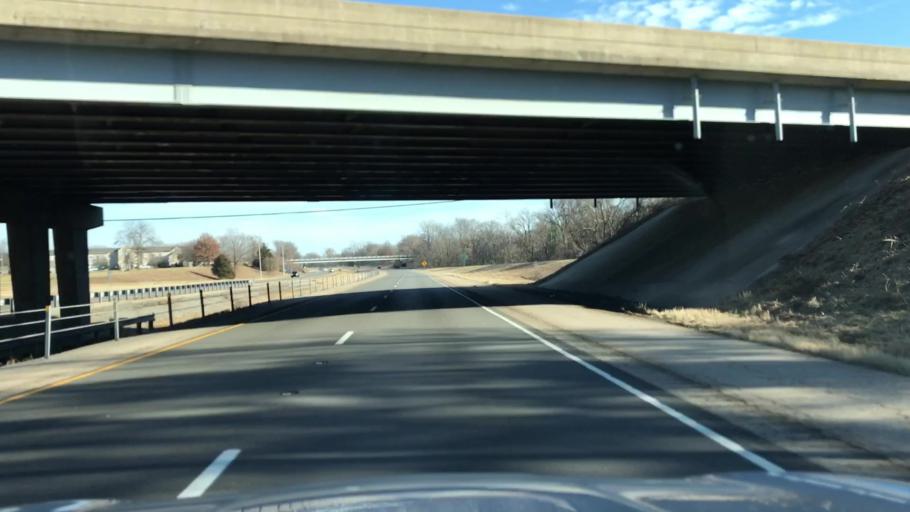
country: US
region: Illinois
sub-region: Madison County
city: Glen Carbon
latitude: 38.7557
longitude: -89.9568
